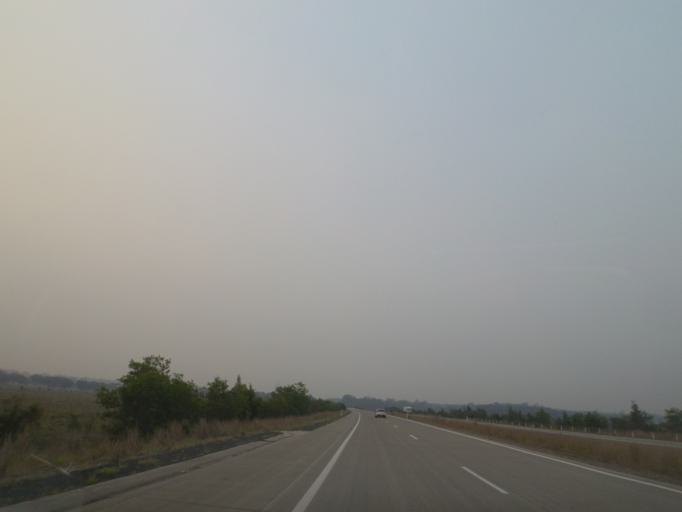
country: AU
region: New South Wales
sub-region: Kempsey
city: Frederickton
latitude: -30.9734
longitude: 152.8590
